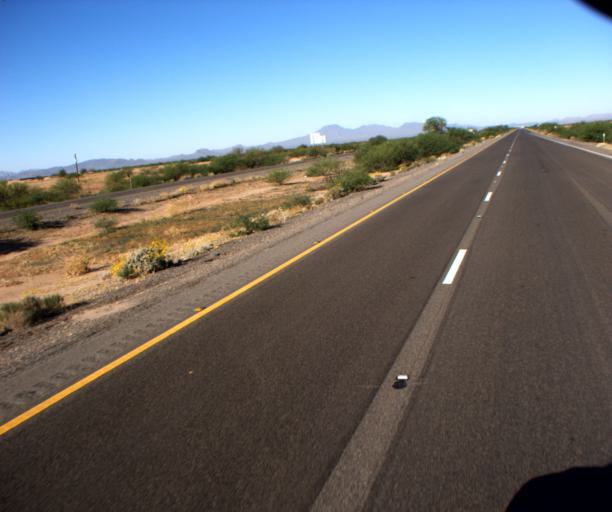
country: US
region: Arizona
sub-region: Pinal County
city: Casa Grande
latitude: 32.8282
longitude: -111.8330
